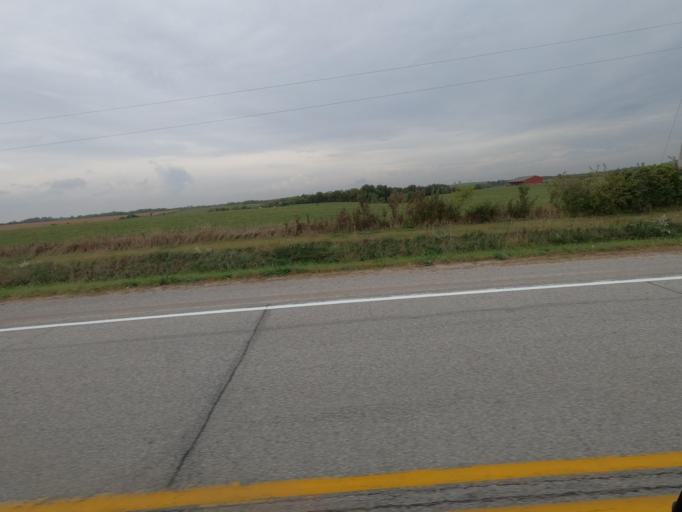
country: US
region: Iowa
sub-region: Van Buren County
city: Keosauqua
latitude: 40.8566
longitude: -92.0659
